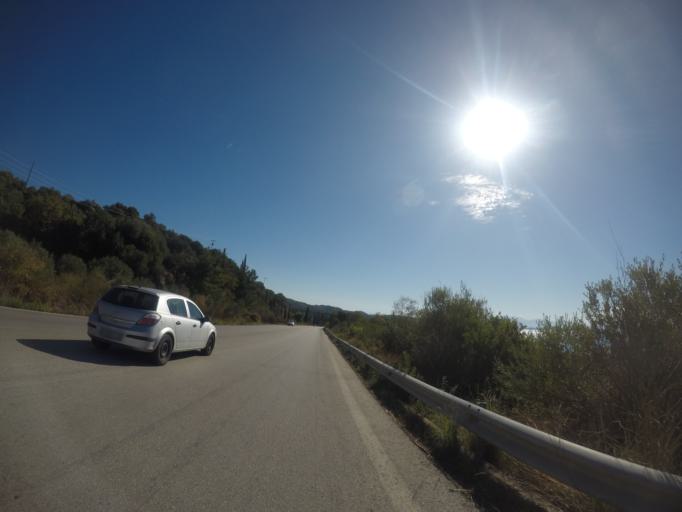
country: GR
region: Epirus
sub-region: Nomos Prevezis
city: Neos Oropos
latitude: 39.1019
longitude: 20.6429
